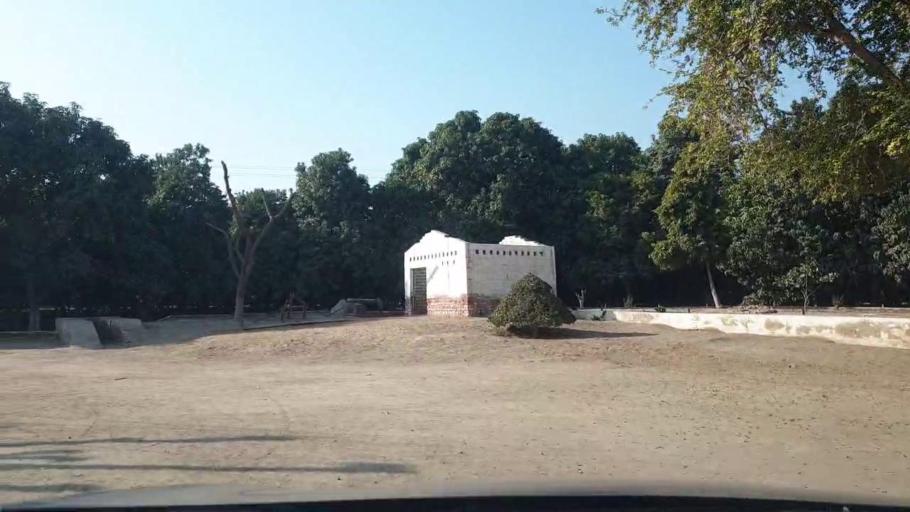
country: PK
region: Sindh
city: Tando Allahyar
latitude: 25.4962
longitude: 68.7089
